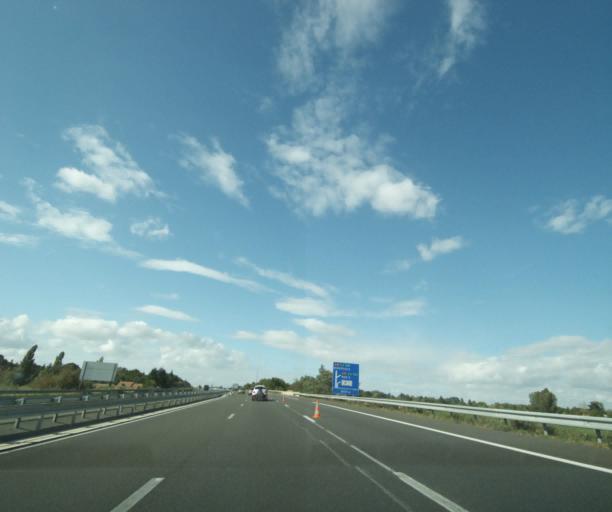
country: FR
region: Centre
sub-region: Departement du Loiret
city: Saint-Pryve-Saint-Mesmin
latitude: 47.8873
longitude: 1.8601
